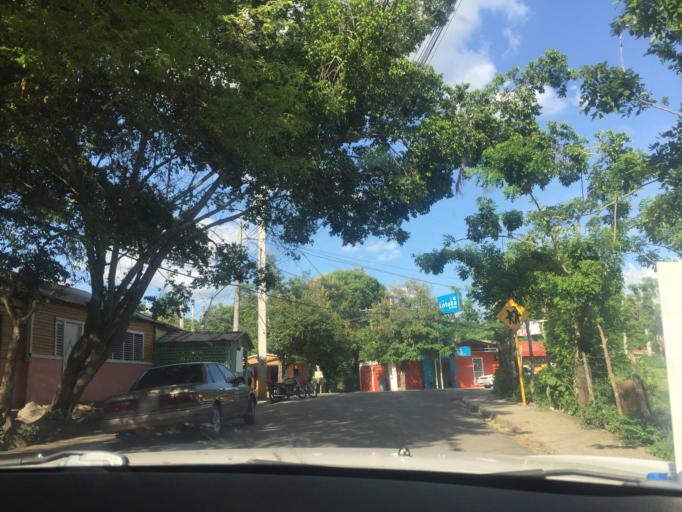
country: DO
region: Santiago
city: Tamboril
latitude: 19.4975
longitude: -70.6349
